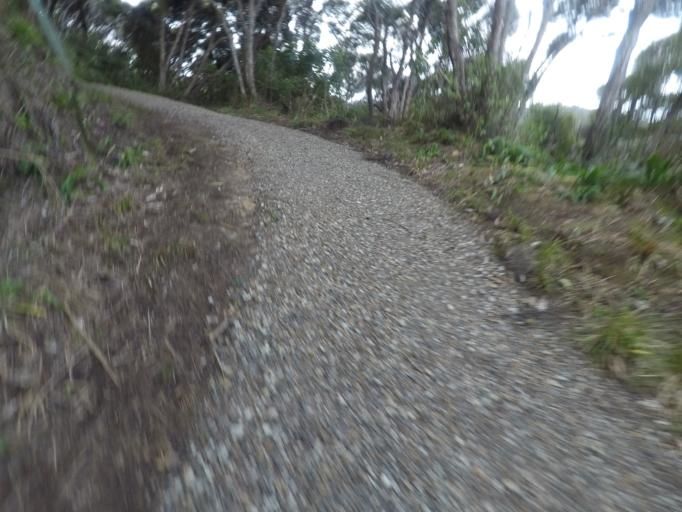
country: NZ
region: Auckland
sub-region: Auckland
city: Muriwai Beach
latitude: -36.9775
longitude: 174.4740
